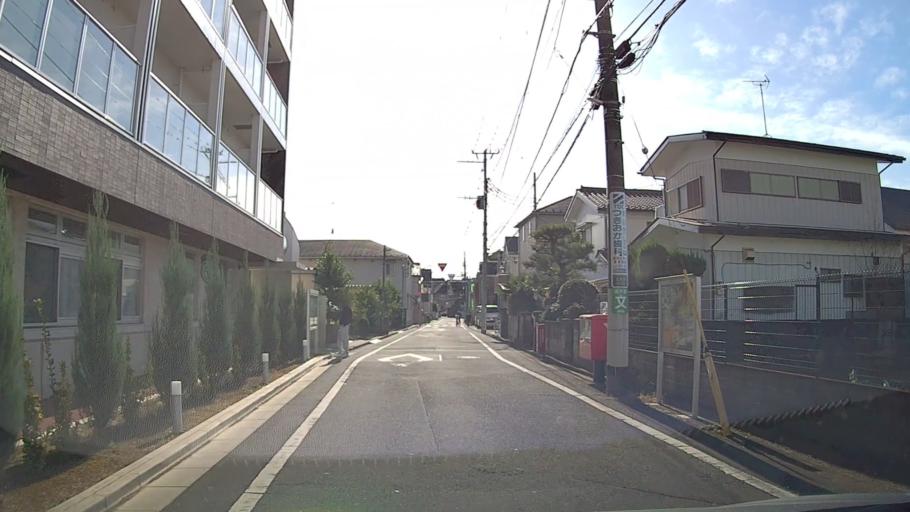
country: JP
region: Saitama
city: Wako
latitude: 35.7639
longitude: 139.6176
